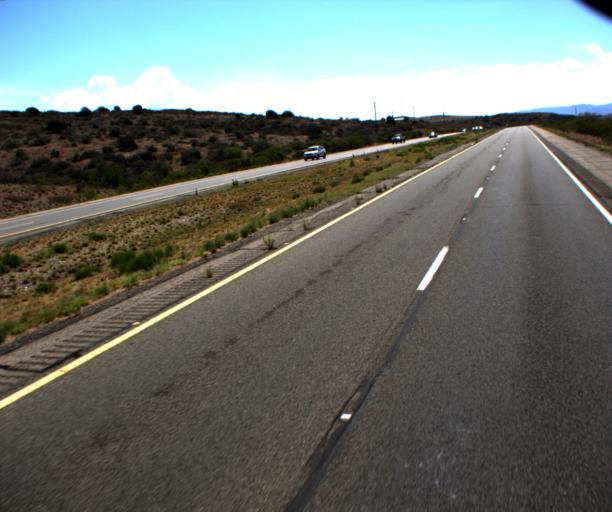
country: US
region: Arizona
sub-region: Yavapai County
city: Spring Valley
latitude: 34.3727
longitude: -112.1869
